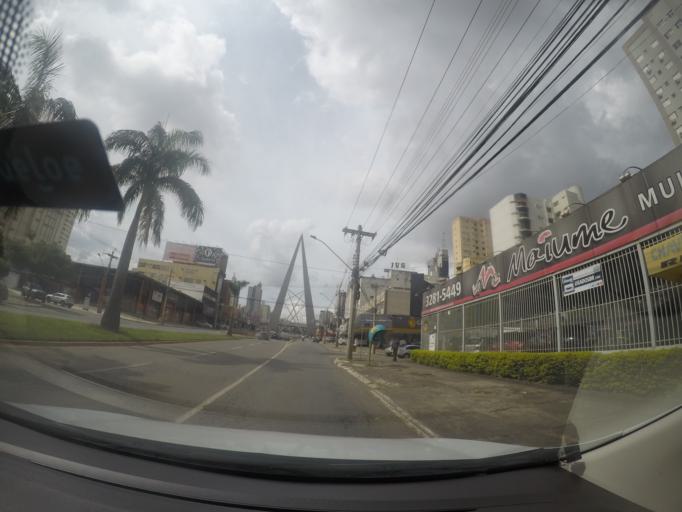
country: BR
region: Goias
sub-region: Goiania
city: Goiania
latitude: -16.7119
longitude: -49.2639
